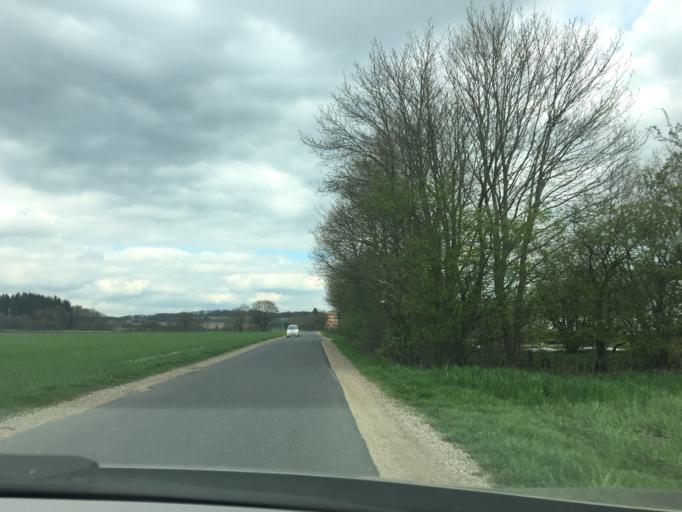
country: DK
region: Central Jutland
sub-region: Horsens Kommune
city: Braedstrup
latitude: 55.9495
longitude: 9.6597
